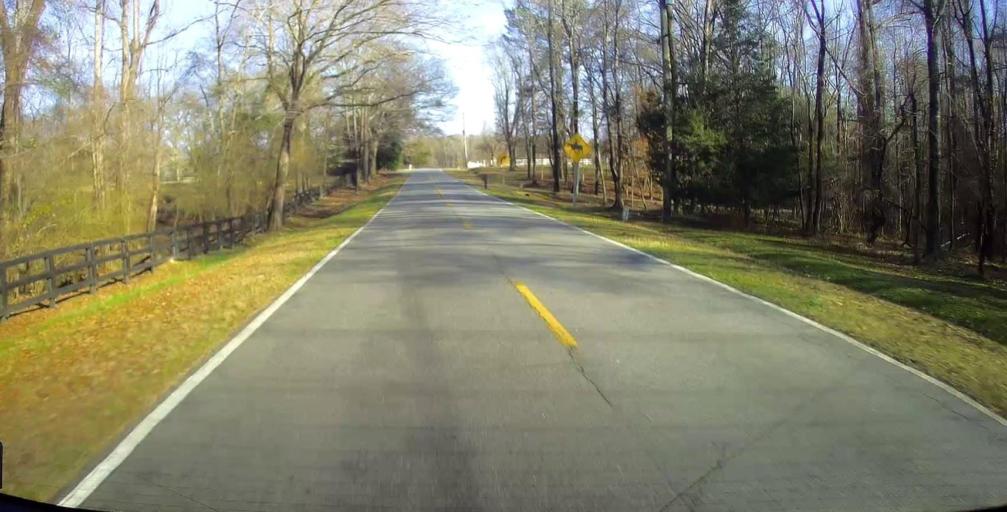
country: US
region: Georgia
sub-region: Harris County
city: Hamilton
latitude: 32.5649
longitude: -84.7959
